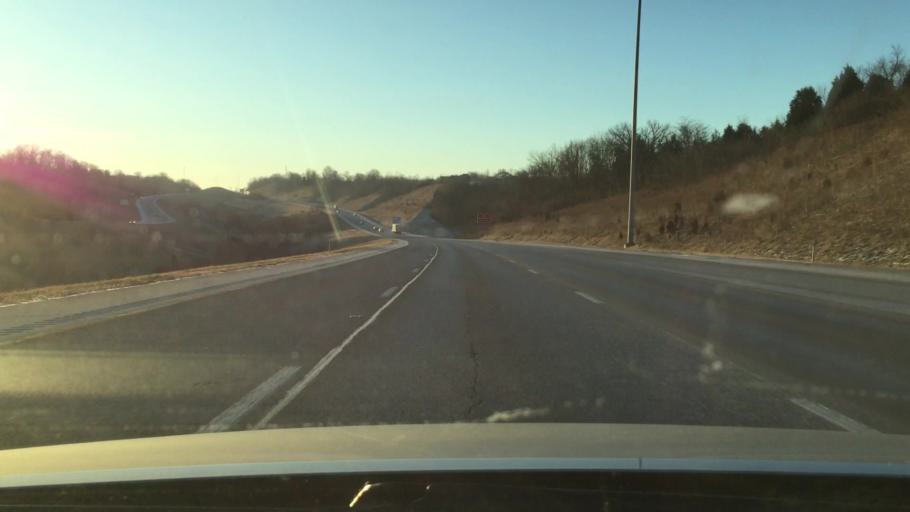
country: US
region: Kentucky
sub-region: Grant County
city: Williamstown
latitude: 38.6415
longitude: -84.5854
